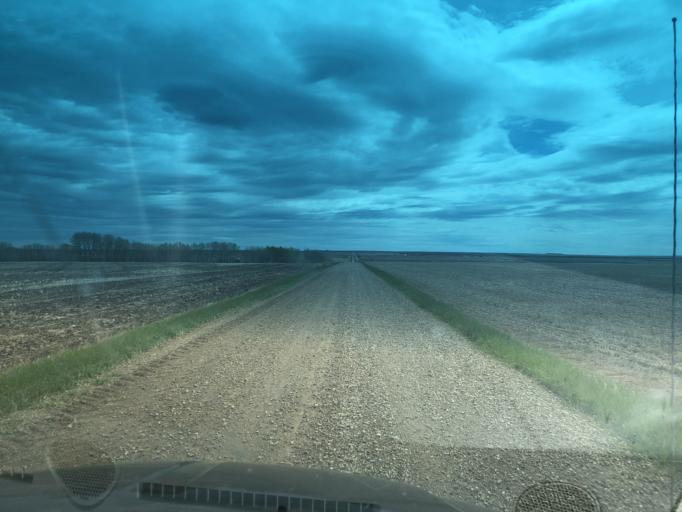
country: CA
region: Alberta
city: Vulcan
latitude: 50.3245
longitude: -113.3547
